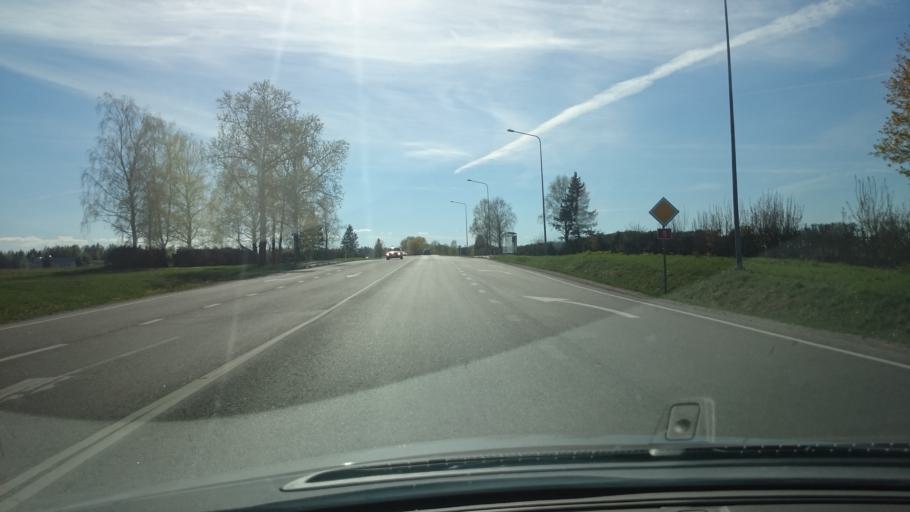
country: EE
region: Laeaene-Virumaa
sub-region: Someru vald
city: Someru
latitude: 59.3656
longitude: 26.4316
